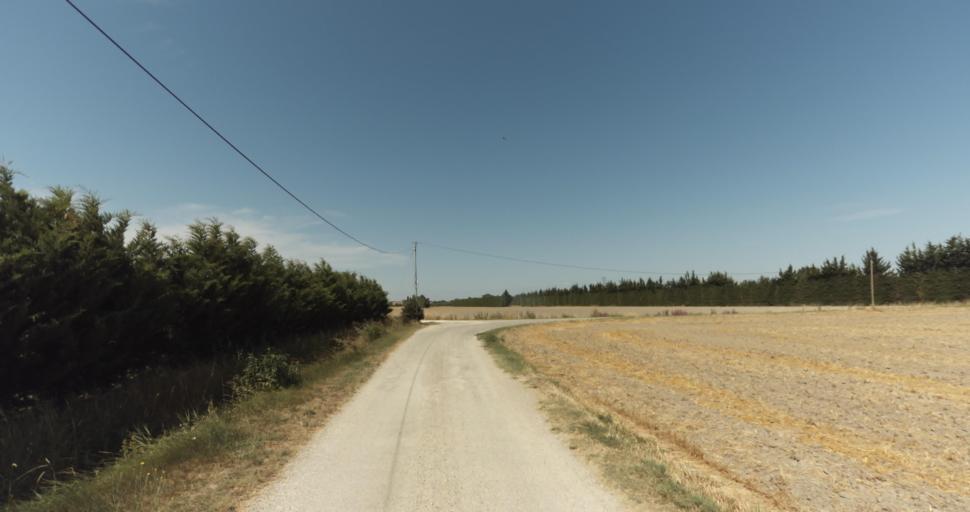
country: FR
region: Provence-Alpes-Cote d'Azur
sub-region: Departement du Vaucluse
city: Monteux
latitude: 44.0064
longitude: 4.9978
